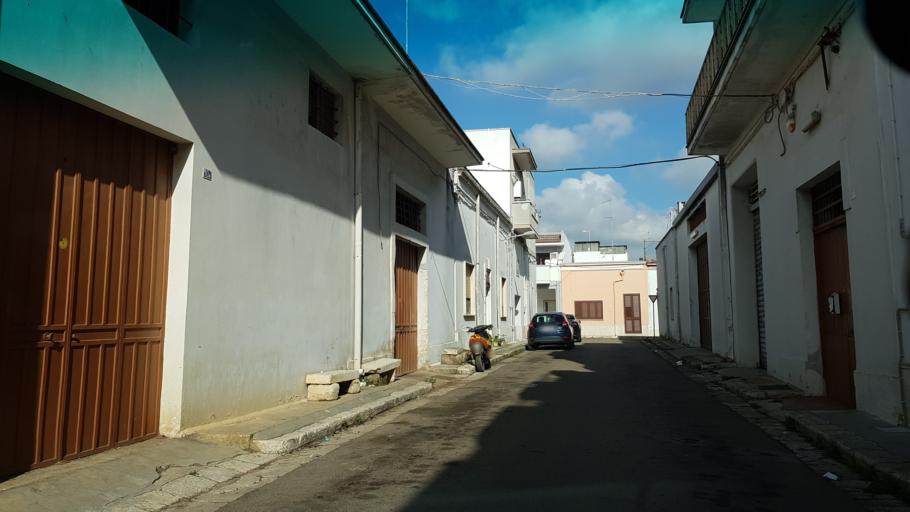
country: IT
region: Apulia
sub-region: Provincia di Brindisi
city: San Pietro Vernotico
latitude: 40.4838
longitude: 18.0000
